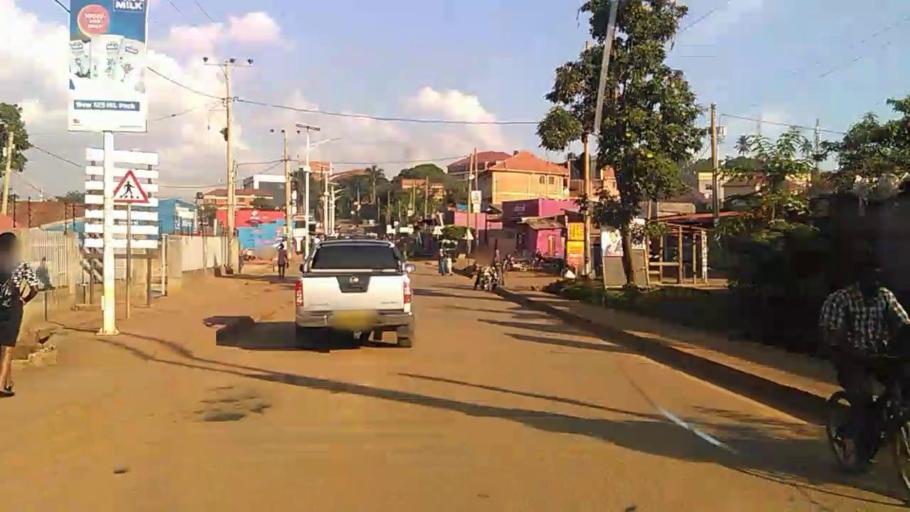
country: UG
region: Central Region
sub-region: Kampala District
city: Kampala
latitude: 0.3074
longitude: 32.5984
